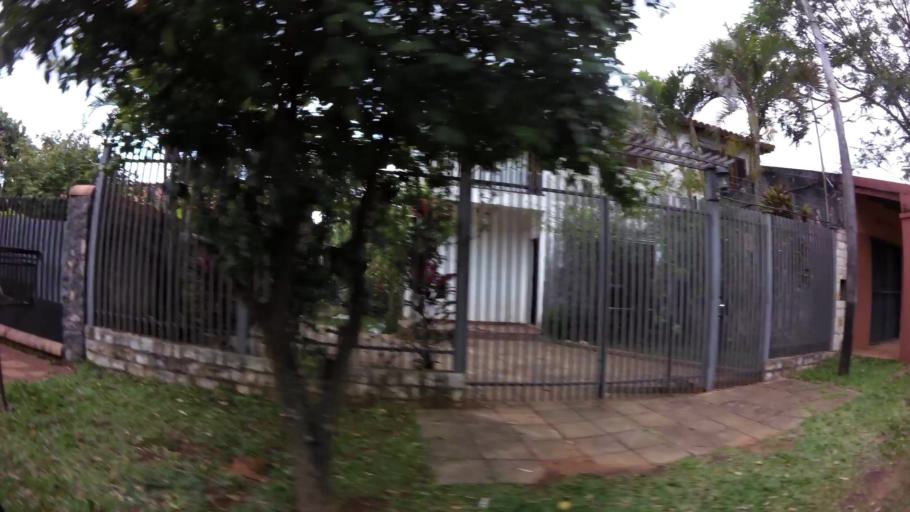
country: PY
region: Central
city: San Lorenzo
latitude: -25.2844
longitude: -57.4972
